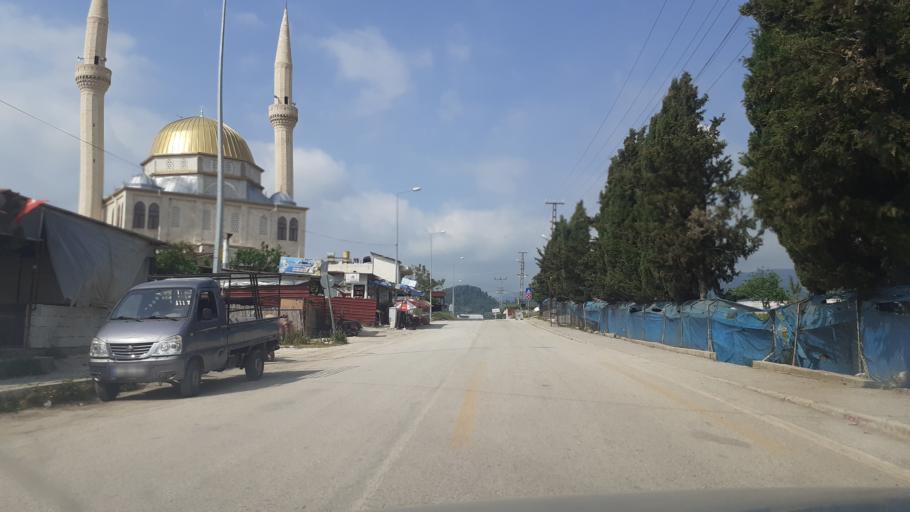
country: TR
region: Hatay
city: Yayladagi
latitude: 35.9079
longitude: 36.0527
